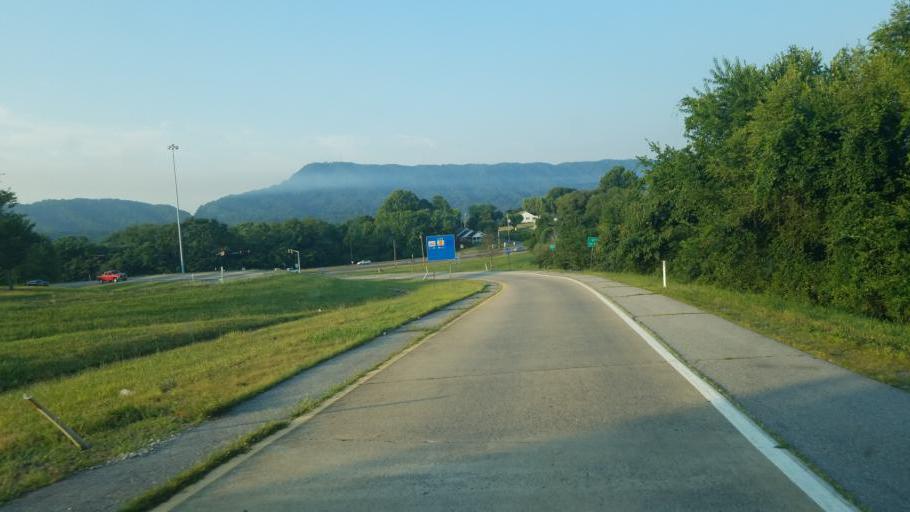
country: US
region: Tennessee
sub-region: Sullivan County
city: Kingsport
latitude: 36.5582
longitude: -82.5844
